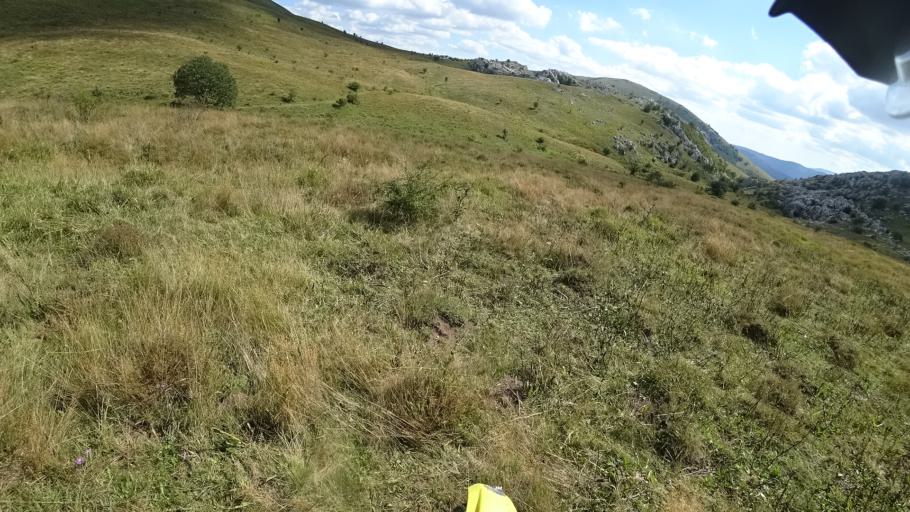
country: HR
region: Zadarska
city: Gracac
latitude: 44.4123
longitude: 16.0003
